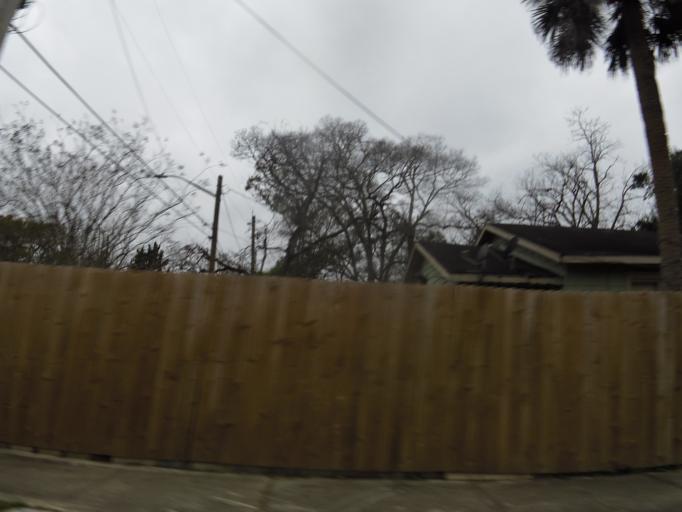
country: US
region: Florida
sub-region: Duval County
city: Jacksonville
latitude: 30.3622
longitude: -81.6848
